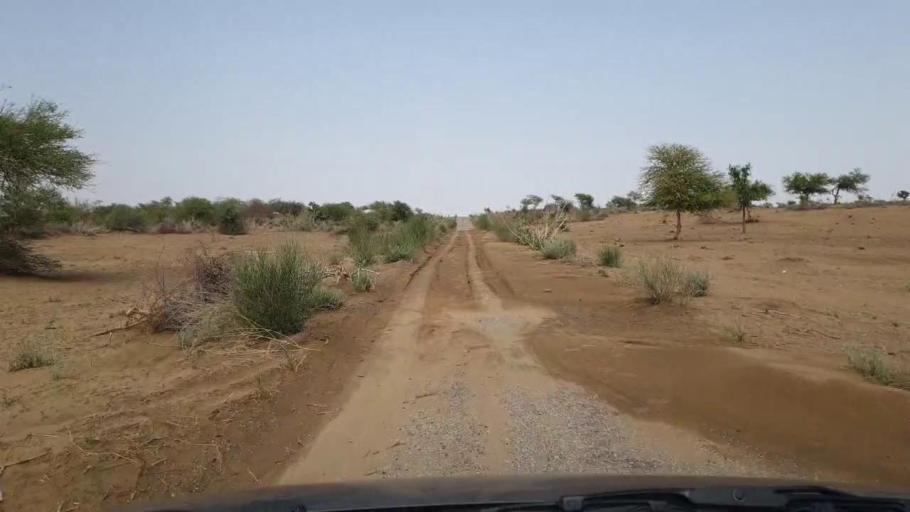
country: PK
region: Sindh
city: Chor
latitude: 25.4818
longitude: 70.5515
